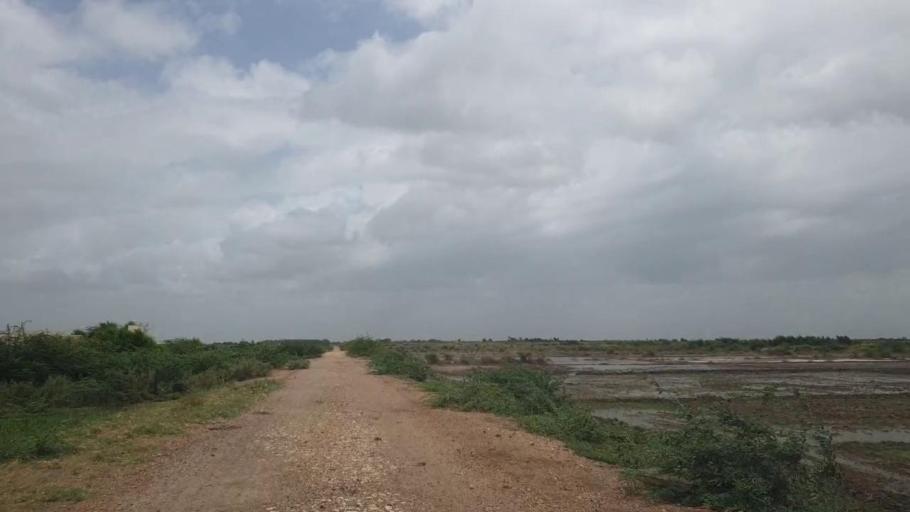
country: PK
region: Sindh
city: Badin
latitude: 24.6267
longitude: 68.9478
